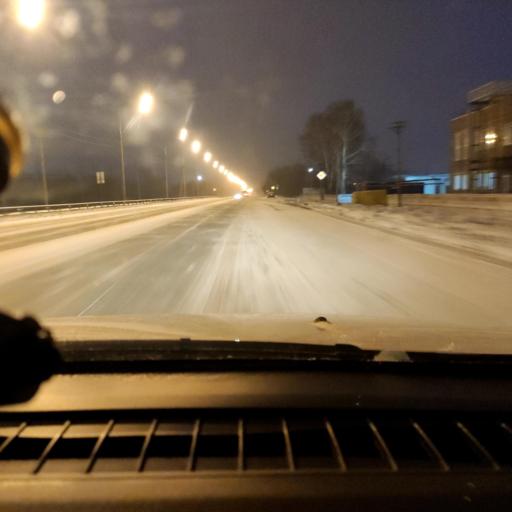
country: RU
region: Samara
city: Otradnyy
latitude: 53.3684
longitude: 51.3615
